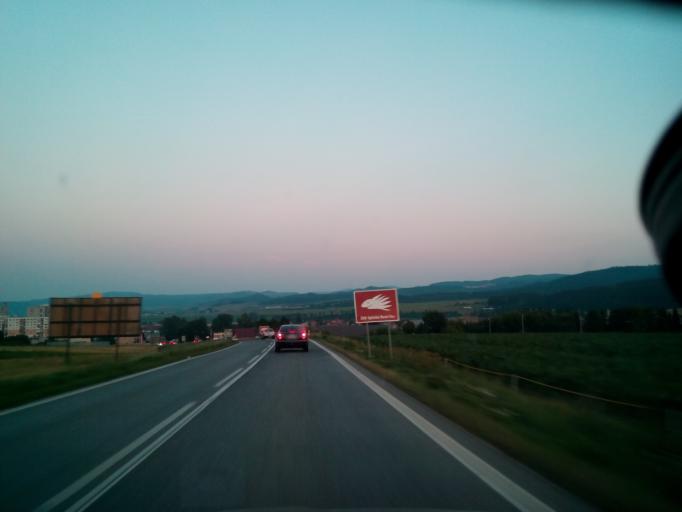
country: SK
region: Kosicky
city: Spisska Nova Ves
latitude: 48.9609
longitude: 20.5059
